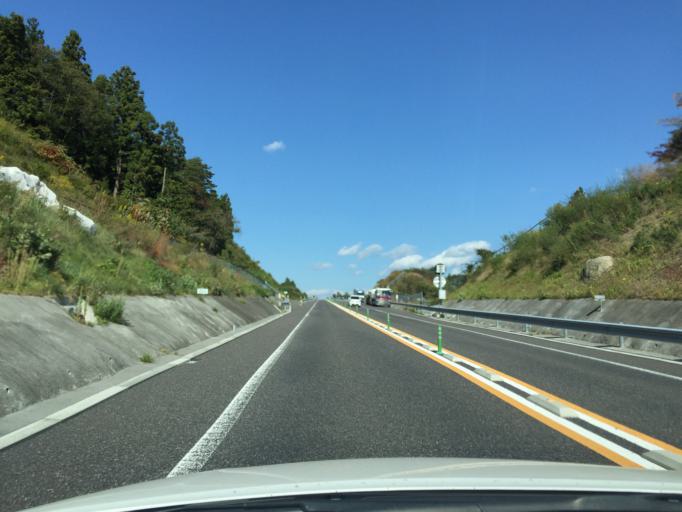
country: JP
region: Fukushima
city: Ishikawa
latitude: 37.2162
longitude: 140.5419
